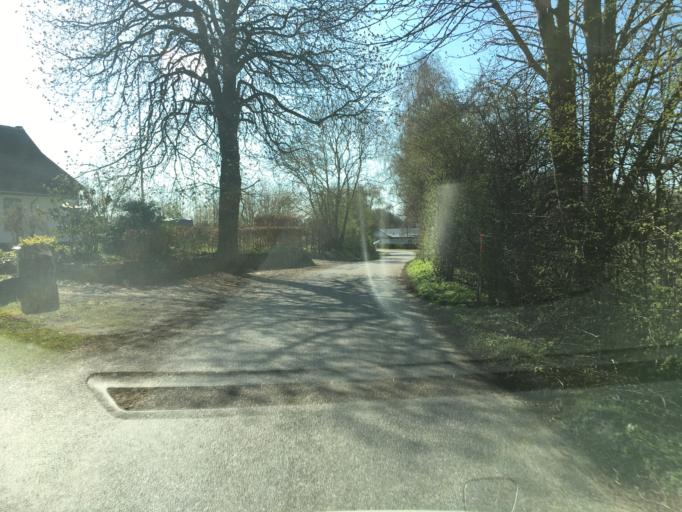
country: DK
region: South Denmark
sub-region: Aabenraa Kommune
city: Krusa
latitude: 54.9198
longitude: 9.4573
